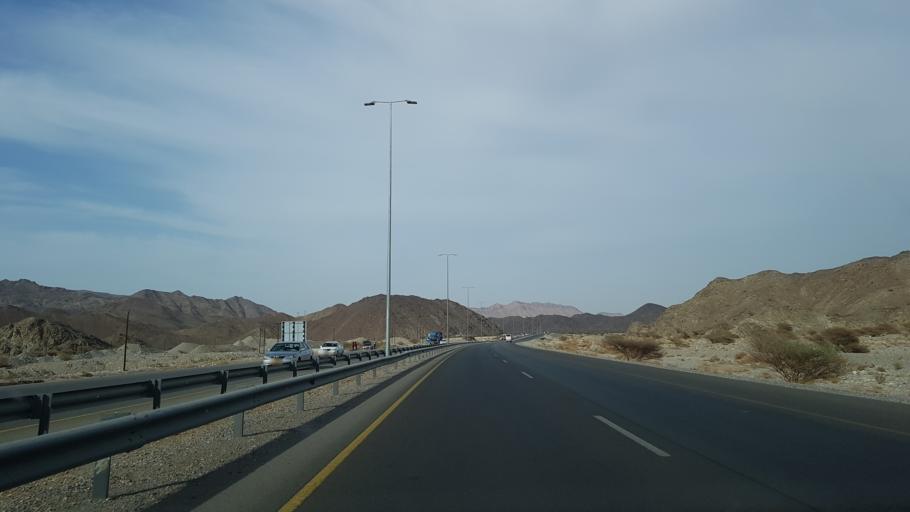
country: OM
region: Muhafazat ad Dakhiliyah
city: Bidbid
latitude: 23.3898
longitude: 58.0626
